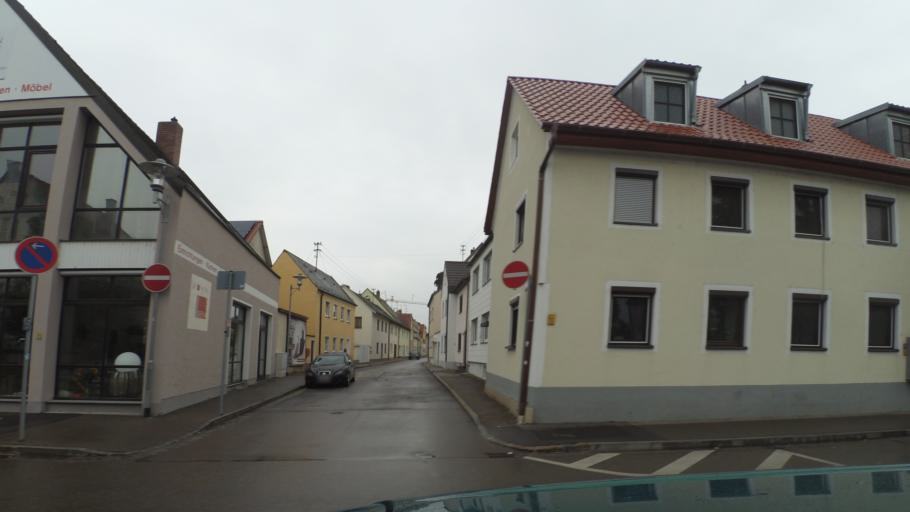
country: DE
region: Bavaria
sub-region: Upper Bavaria
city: Neuburg an der Donau
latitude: 48.7331
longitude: 11.1839
